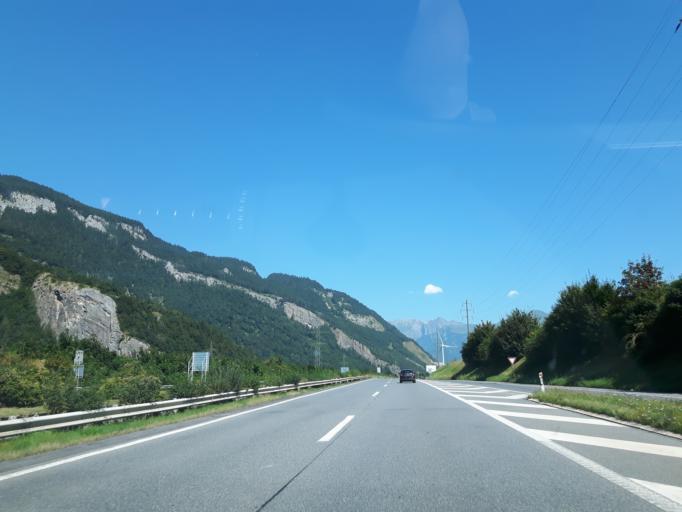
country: CH
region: Grisons
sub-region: Plessur District
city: Chur
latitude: 46.8781
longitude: 9.5343
